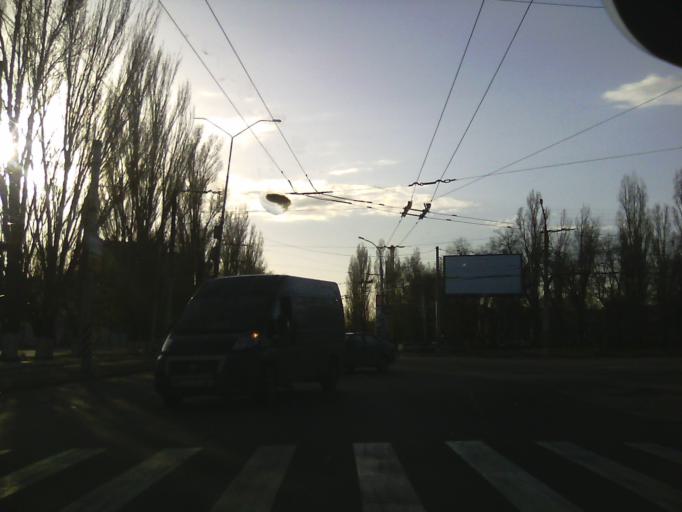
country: RU
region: Saratov
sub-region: Saratovskiy Rayon
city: Saratov
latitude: 51.5909
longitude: 45.9497
